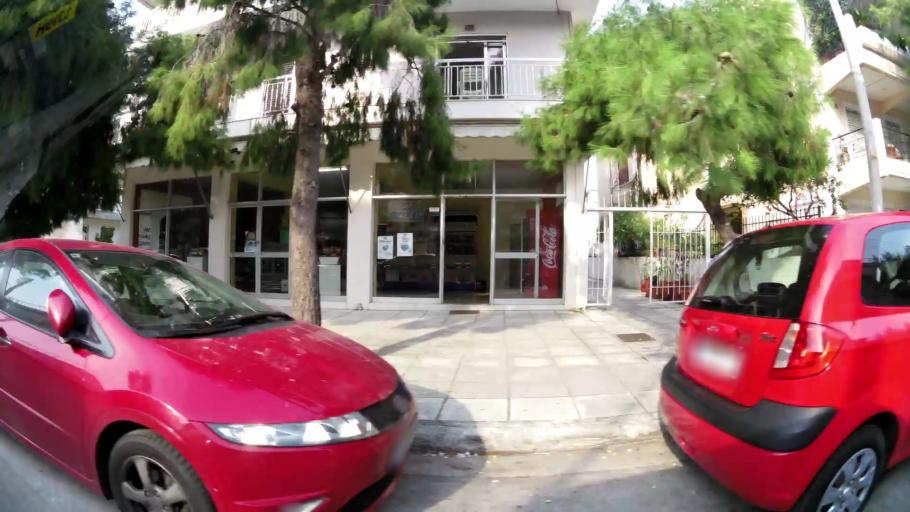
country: GR
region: Attica
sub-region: Nomarchia Athinas
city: Agios Dimitrios
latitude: 37.9286
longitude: 23.7178
